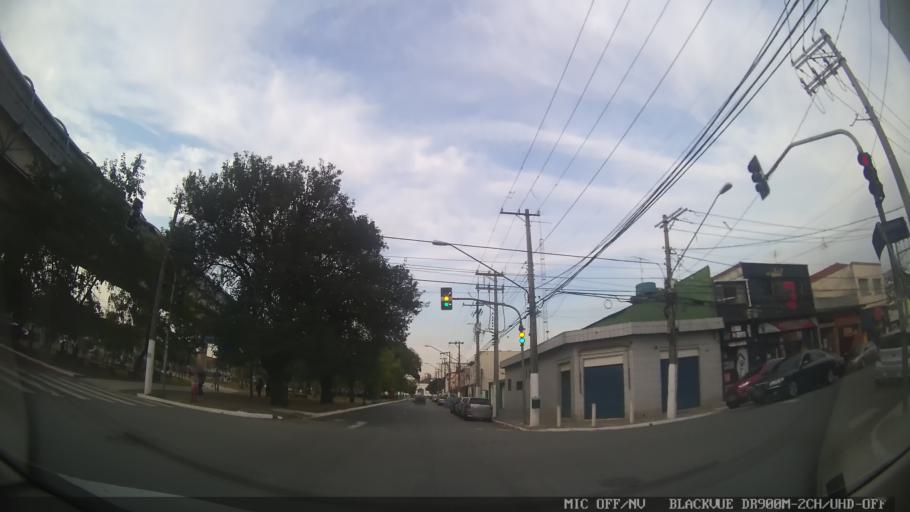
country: BR
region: Sao Paulo
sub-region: Sao Caetano Do Sul
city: Sao Caetano do Sul
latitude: -23.5956
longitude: -46.5917
